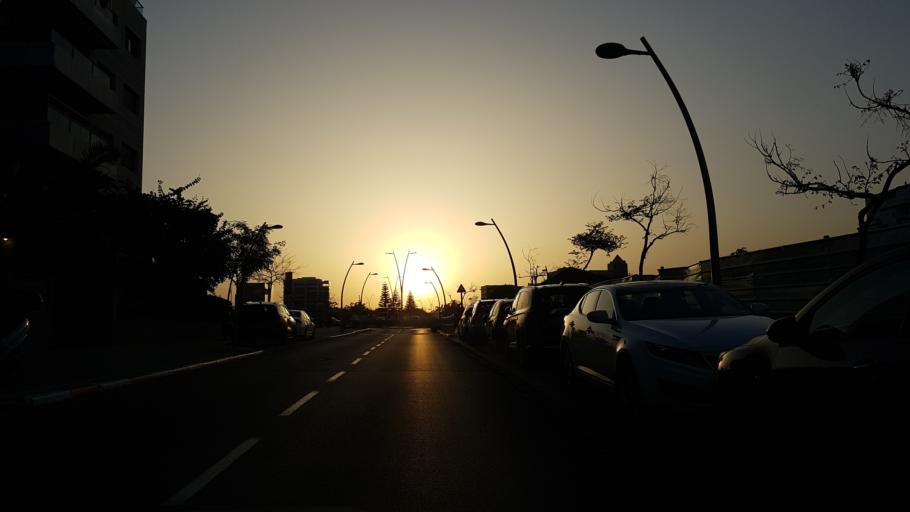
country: IL
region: Central District
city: Ra'anana
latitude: 32.1947
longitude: 34.8909
